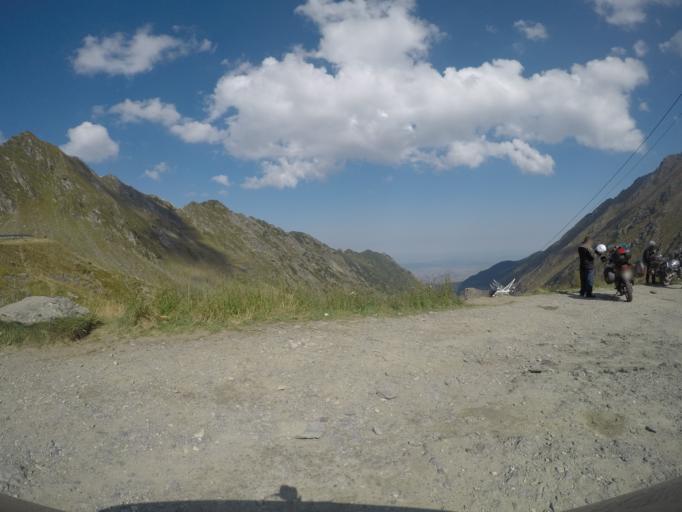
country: RO
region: Sibiu
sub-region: Comuna Cartisoara
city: Cartisoara
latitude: 45.6054
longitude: 24.6160
